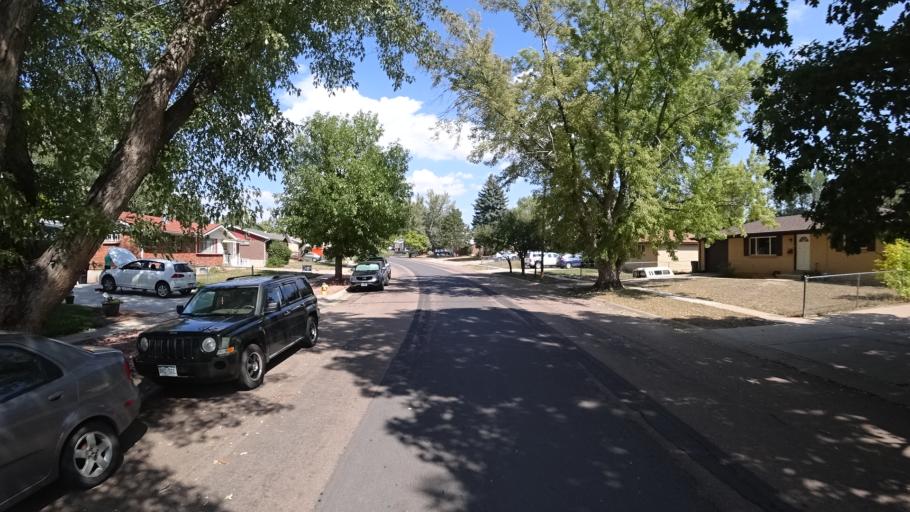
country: US
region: Colorado
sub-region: El Paso County
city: Colorado Springs
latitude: 38.8305
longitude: -104.7678
